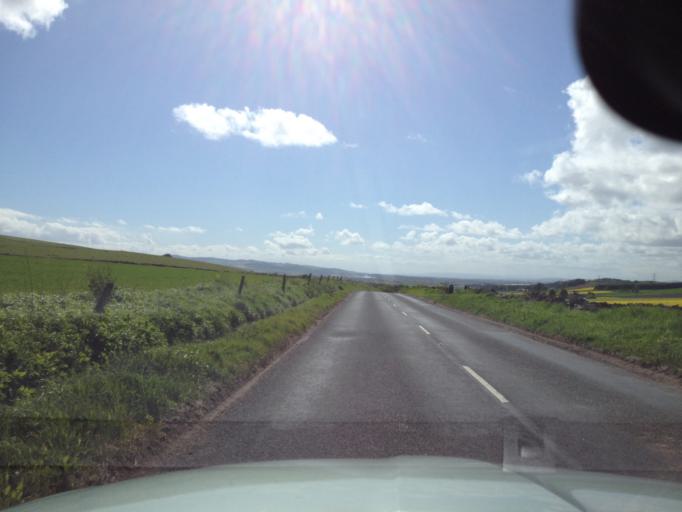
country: GB
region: Scotland
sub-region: Angus
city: Letham
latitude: 56.6775
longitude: -2.8137
